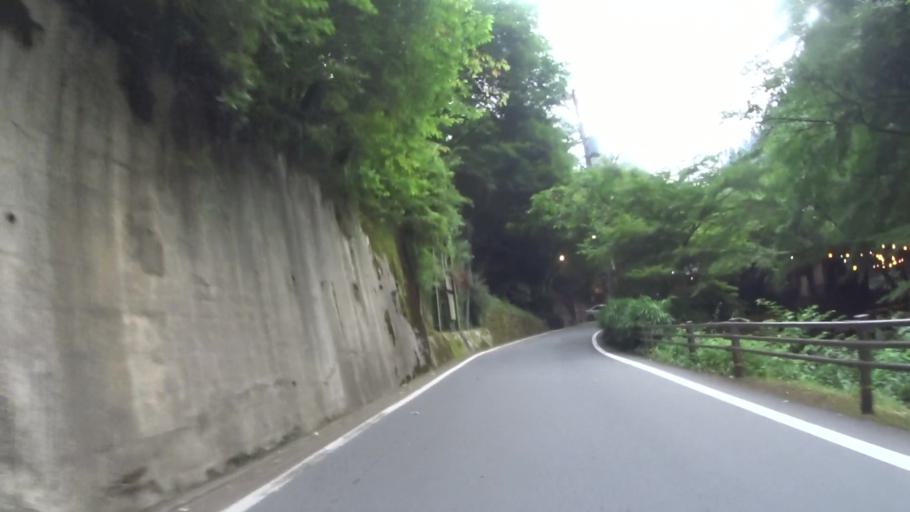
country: JP
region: Kyoto
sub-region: Kyoto-shi
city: Kamigyo-ku
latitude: 35.1165
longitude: 135.7606
